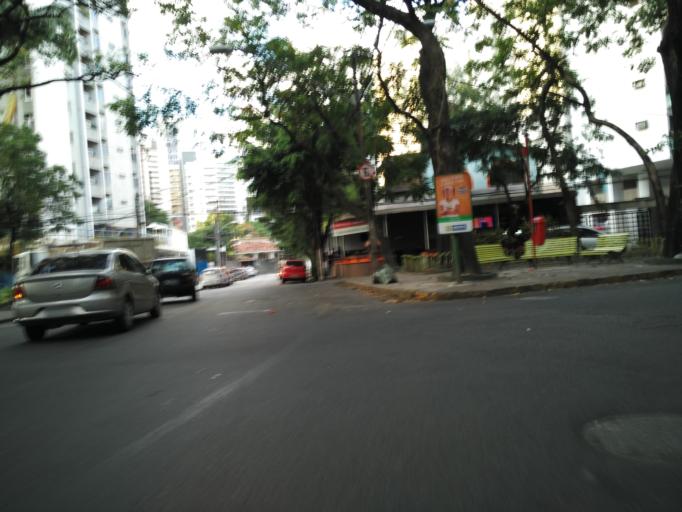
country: BR
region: Pernambuco
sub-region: Recife
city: Recife
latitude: -8.0329
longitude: -34.9072
